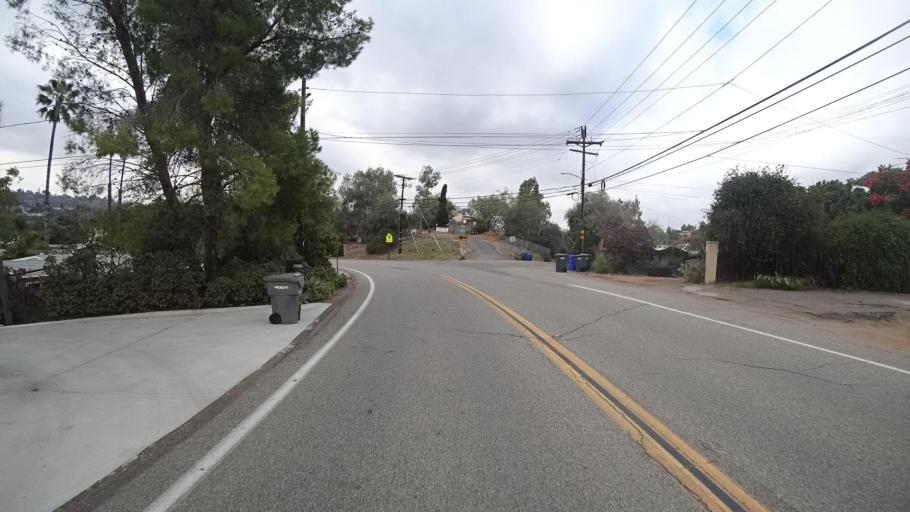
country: US
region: California
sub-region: San Diego County
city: Spring Valley
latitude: 32.7528
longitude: -116.9871
